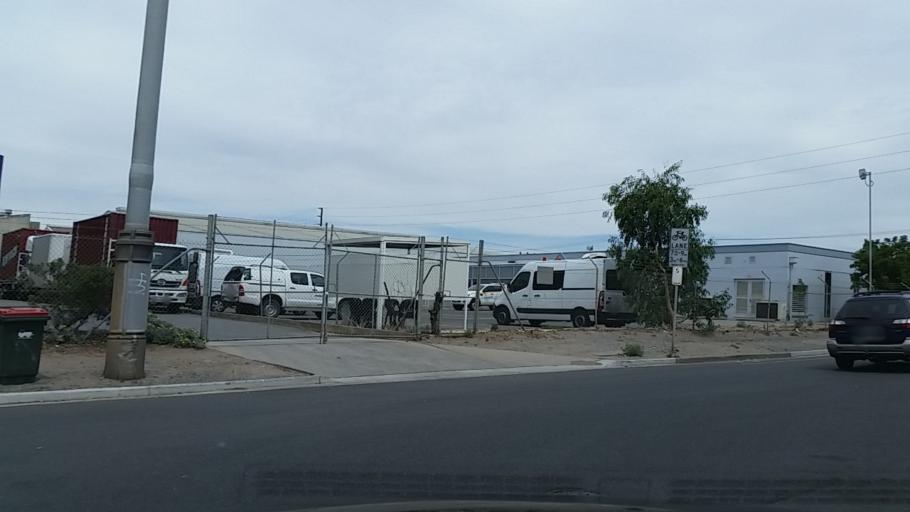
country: AU
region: South Australia
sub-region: City of West Torrens
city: Plympton
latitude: -34.9580
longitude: 138.5365
